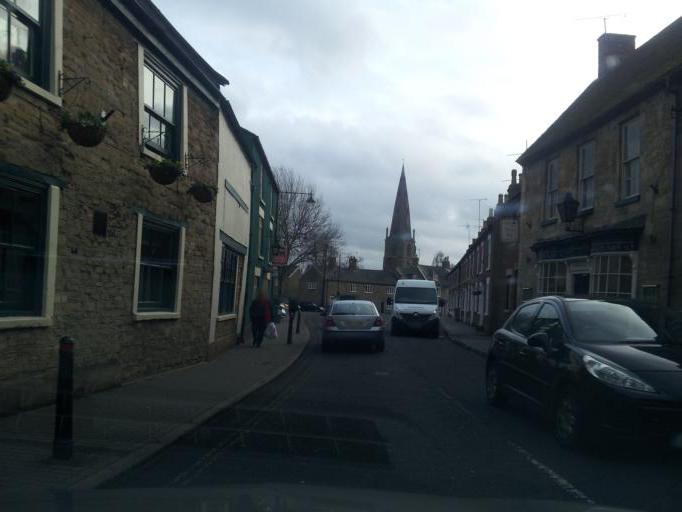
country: GB
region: England
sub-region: Milton Keynes
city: Olney
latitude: 52.1519
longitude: -0.7020
